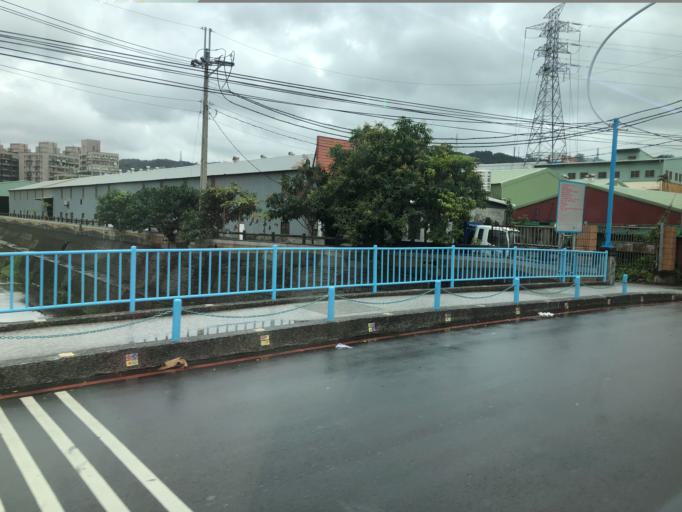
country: TW
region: Taipei
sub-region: Taipei
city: Banqiao
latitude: 25.0278
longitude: 121.4265
